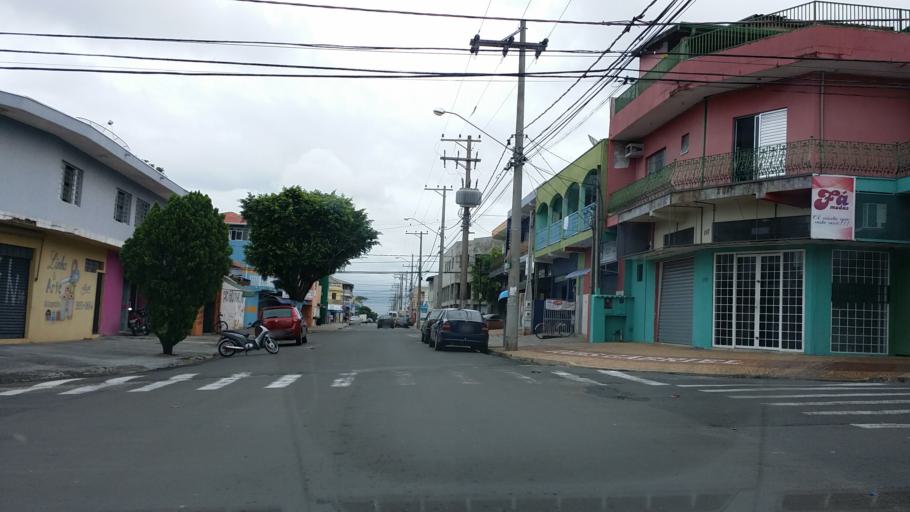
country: BR
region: Sao Paulo
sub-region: Indaiatuba
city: Indaiatuba
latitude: -23.1235
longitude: -47.2411
